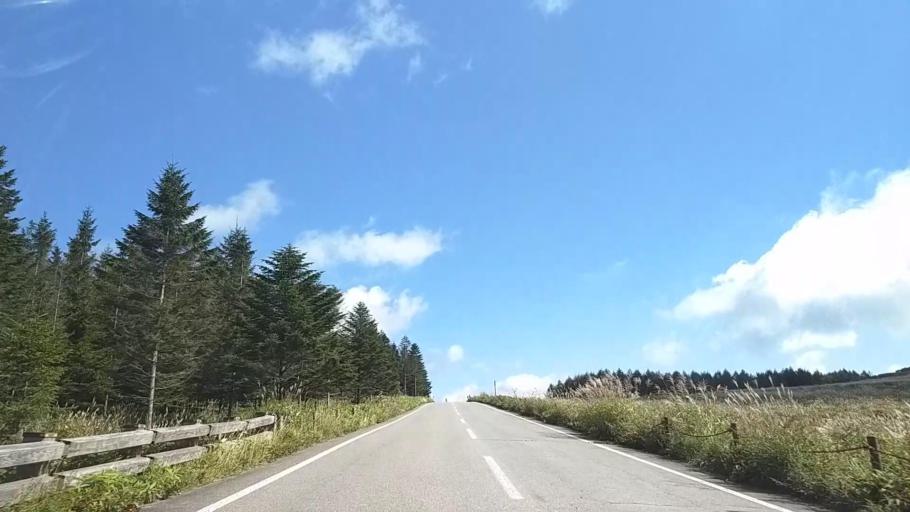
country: JP
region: Nagano
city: Suwa
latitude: 36.1006
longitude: 138.1696
